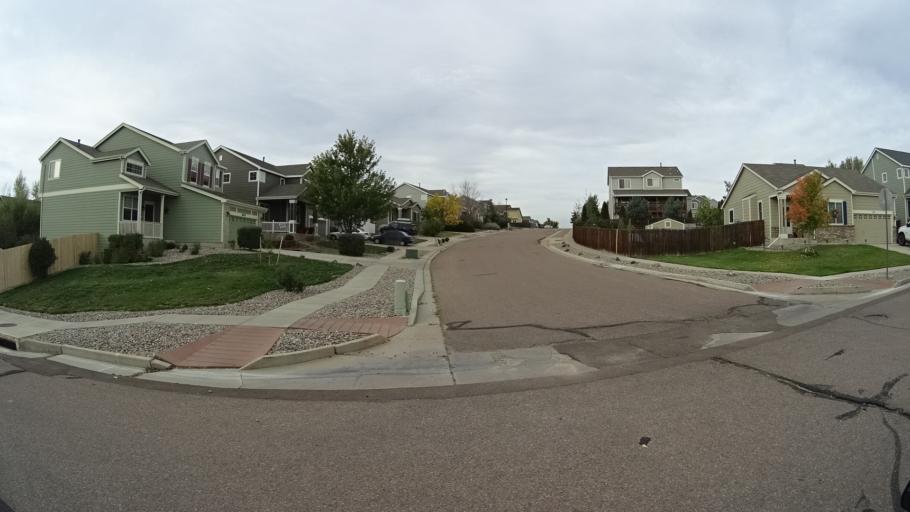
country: US
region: Colorado
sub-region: El Paso County
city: Cimarron Hills
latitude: 38.9232
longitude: -104.7067
